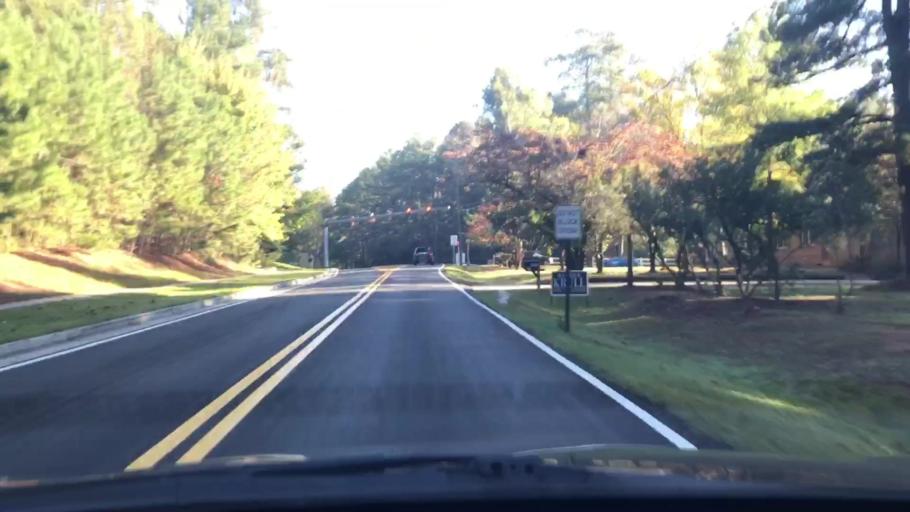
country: US
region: Georgia
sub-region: Douglas County
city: Douglasville
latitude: 33.7345
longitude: -84.7584
